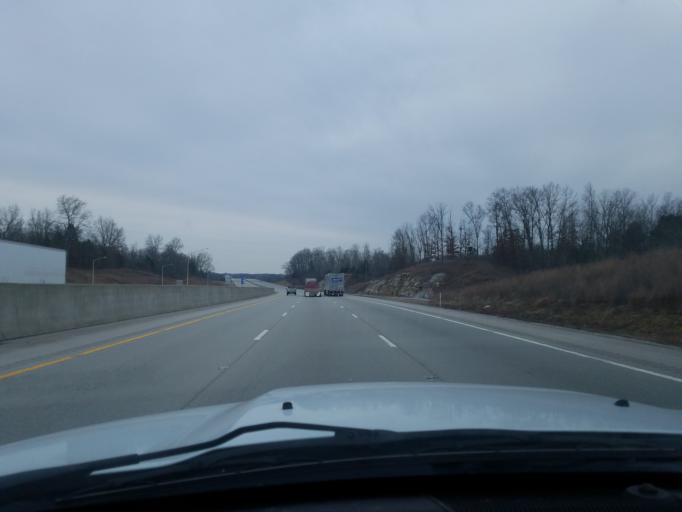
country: US
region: Kentucky
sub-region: Barren County
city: Cave City
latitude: 37.0969
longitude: -86.0559
